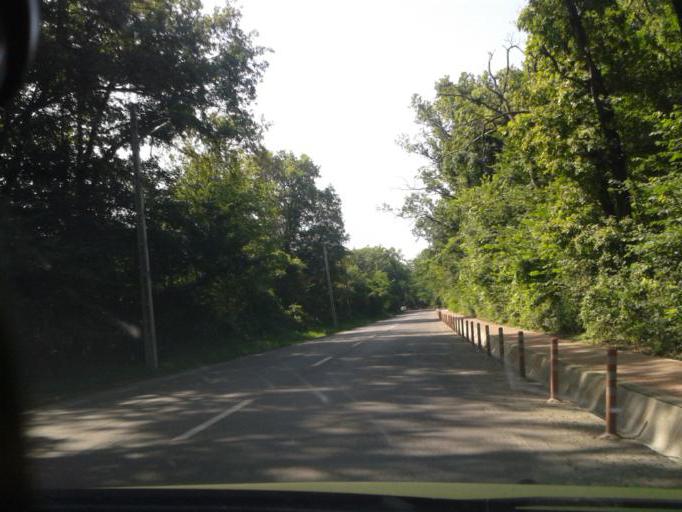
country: RO
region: Prahova
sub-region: Comuna Paulesti
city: Gageni
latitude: 45.0136
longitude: 25.9514
